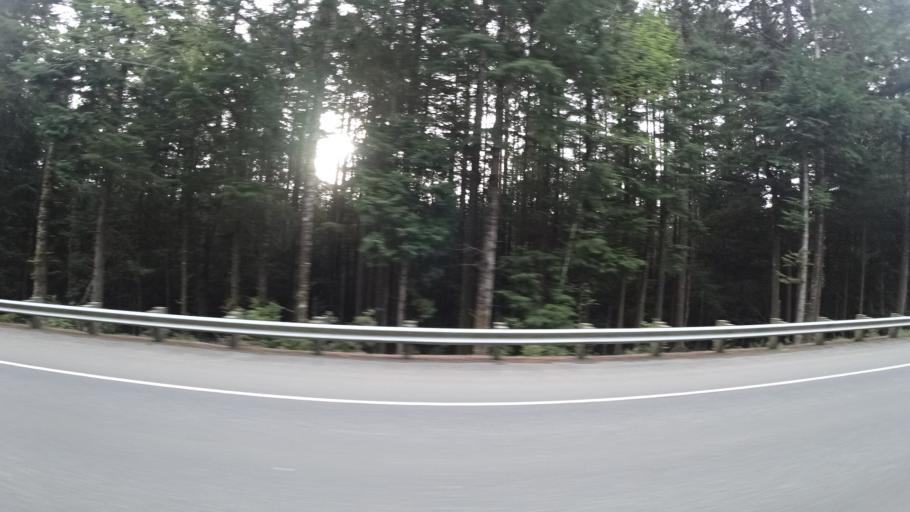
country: US
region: Oregon
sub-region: Coos County
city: Barview
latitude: 43.2468
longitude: -124.2872
